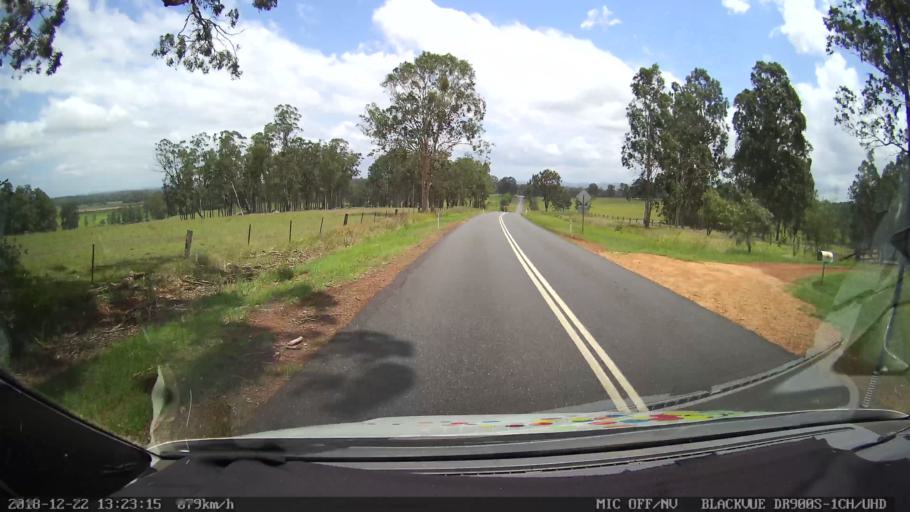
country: AU
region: New South Wales
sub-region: Clarence Valley
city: Coutts Crossing
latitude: -29.7960
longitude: 152.9086
